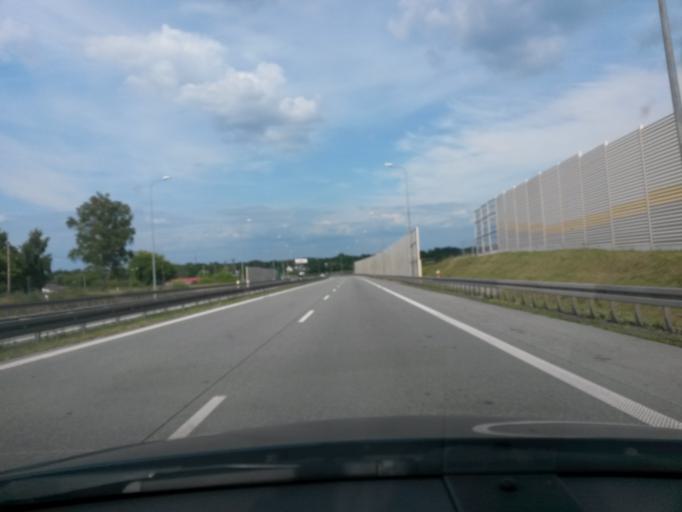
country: PL
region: Lodz Voivodeship
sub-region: Powiat skierniewicki
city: Kowiesy
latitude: 51.8831
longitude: 20.4086
